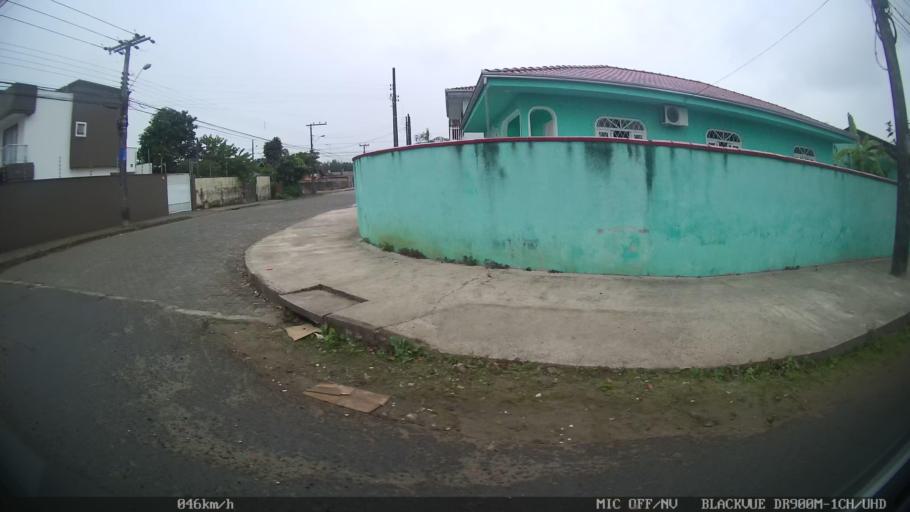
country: BR
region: Santa Catarina
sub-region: Joinville
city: Joinville
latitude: -26.2704
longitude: -48.7982
